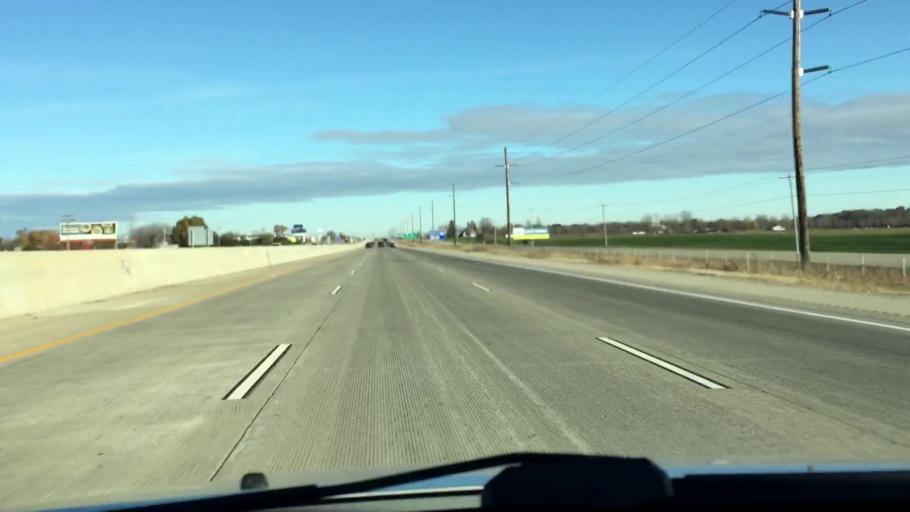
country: US
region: Wisconsin
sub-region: Winnebago County
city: Oshkosh
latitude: 43.9682
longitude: -88.5829
